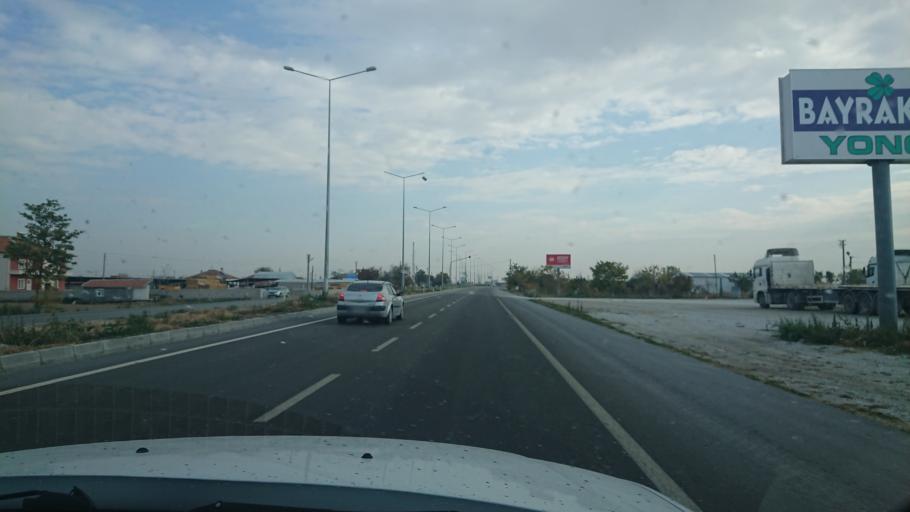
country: TR
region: Aksaray
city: Yesilova
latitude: 38.2899
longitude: 33.7552
